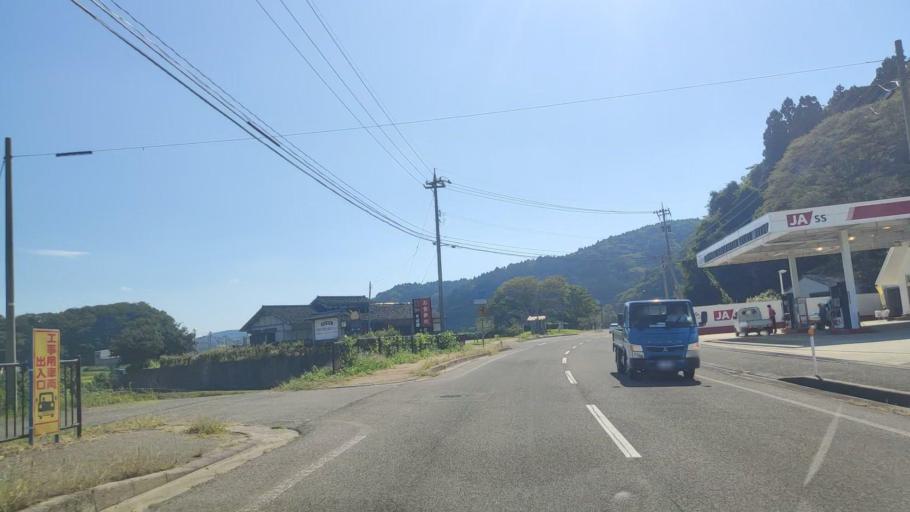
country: JP
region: Ishikawa
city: Nanao
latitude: 37.2907
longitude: 136.7511
